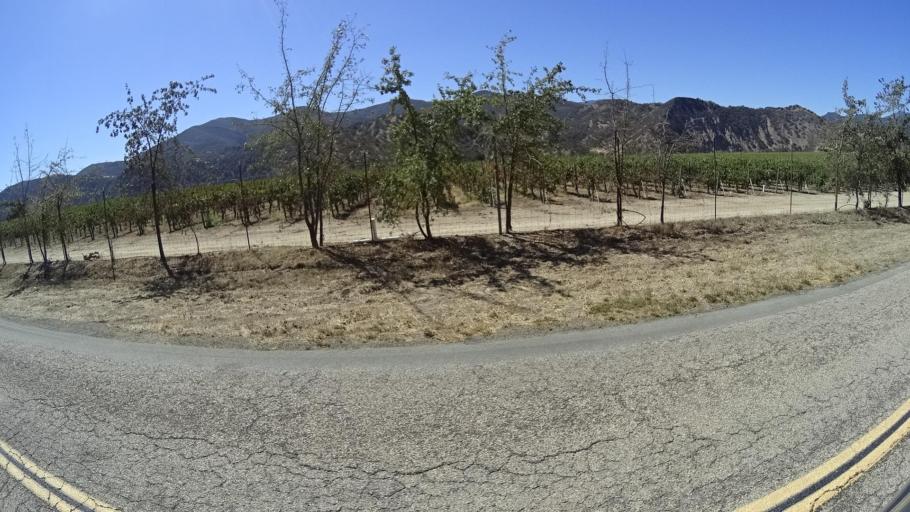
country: US
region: California
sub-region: Monterey County
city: Greenfield
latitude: 36.2700
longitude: -121.3807
